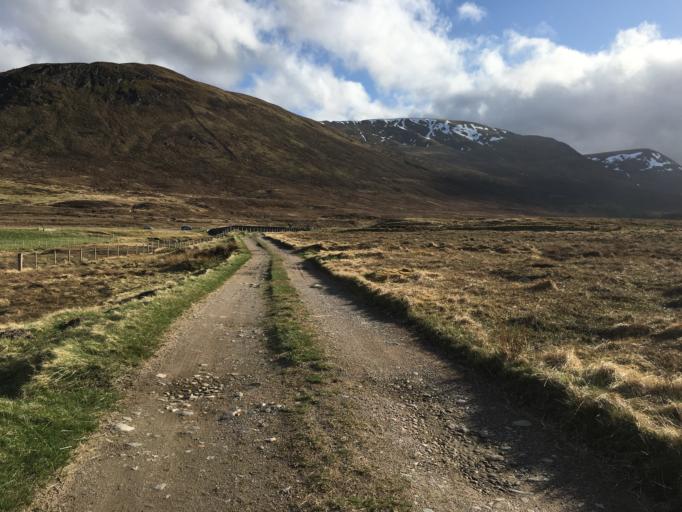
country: GB
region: Scotland
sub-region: Highland
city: Kingussie
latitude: 57.0225
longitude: -4.4351
